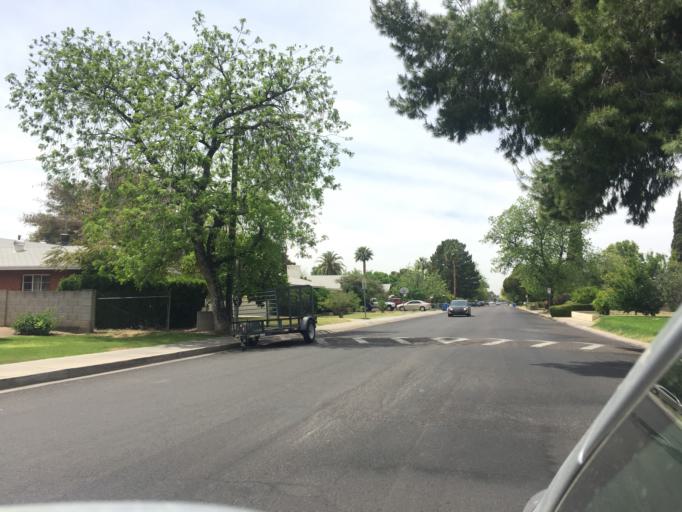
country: US
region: Arizona
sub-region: Maricopa County
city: Phoenix
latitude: 33.5273
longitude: -112.0484
